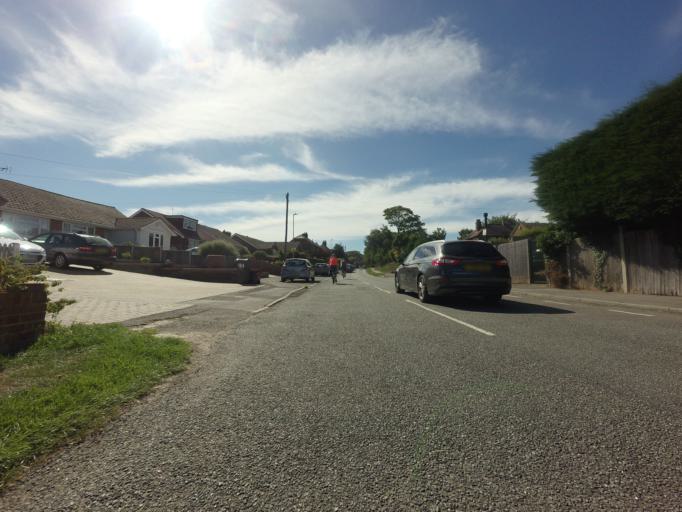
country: GB
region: England
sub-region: Kent
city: Birchington-on-Sea
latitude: 51.3404
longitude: 1.2747
